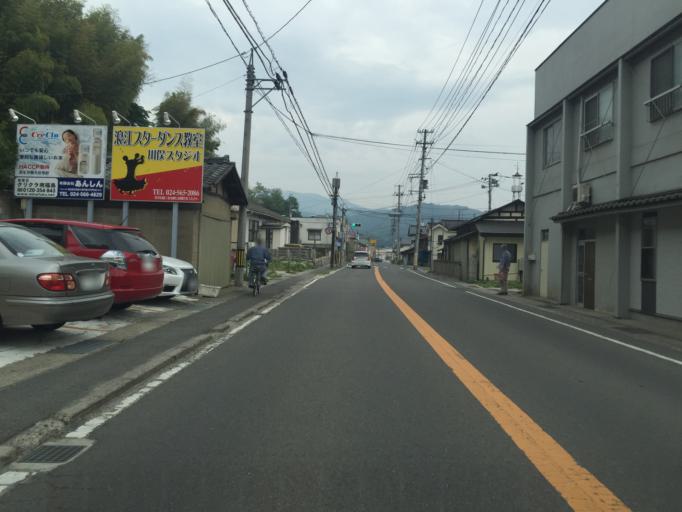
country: JP
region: Fukushima
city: Fukushima-shi
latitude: 37.6666
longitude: 140.5918
